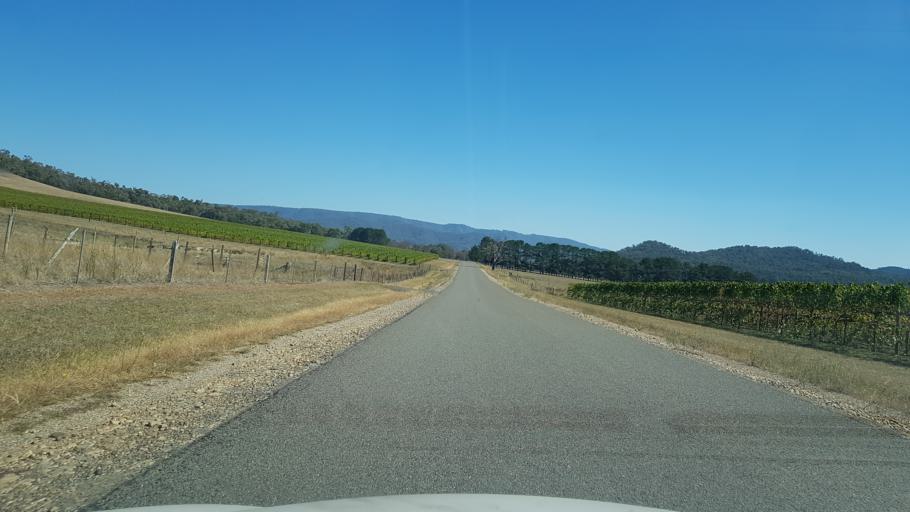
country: AU
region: Victoria
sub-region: Mansfield
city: Mansfield
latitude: -36.8184
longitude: 146.4765
